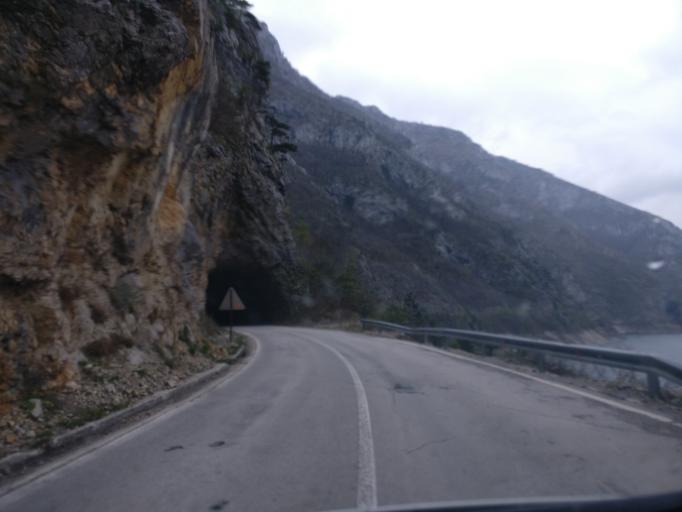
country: ME
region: Opstina Pluzine
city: Pluzine
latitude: 43.2438
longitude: 18.8365
